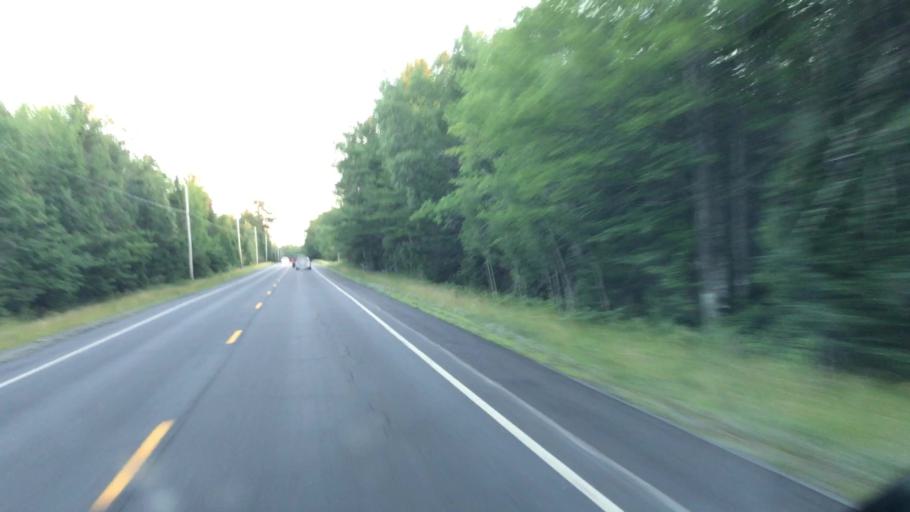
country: US
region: Maine
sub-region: Penobscot County
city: Medway
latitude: 45.5827
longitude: -68.3168
